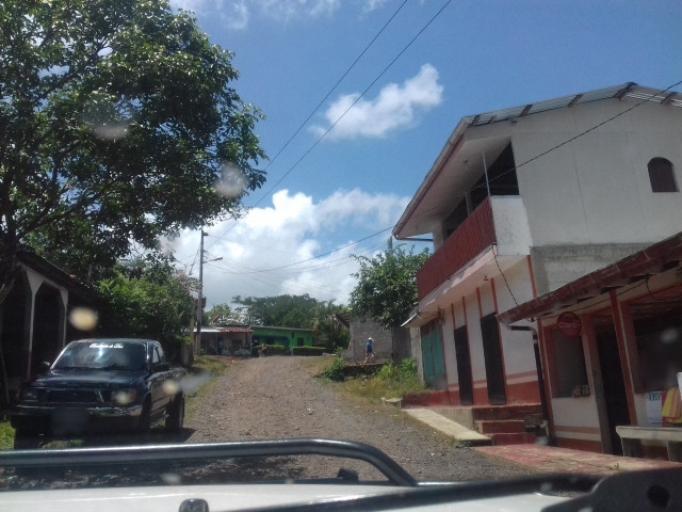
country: NI
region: Matagalpa
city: Rio Blanco
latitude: 12.9792
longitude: -85.3615
